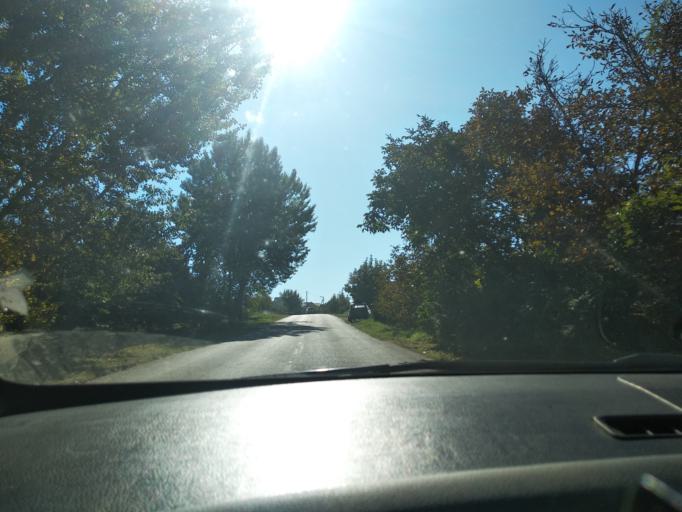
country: RU
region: Krasnodarskiy
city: Goryachiy Klyuch
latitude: 44.6242
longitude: 39.1579
